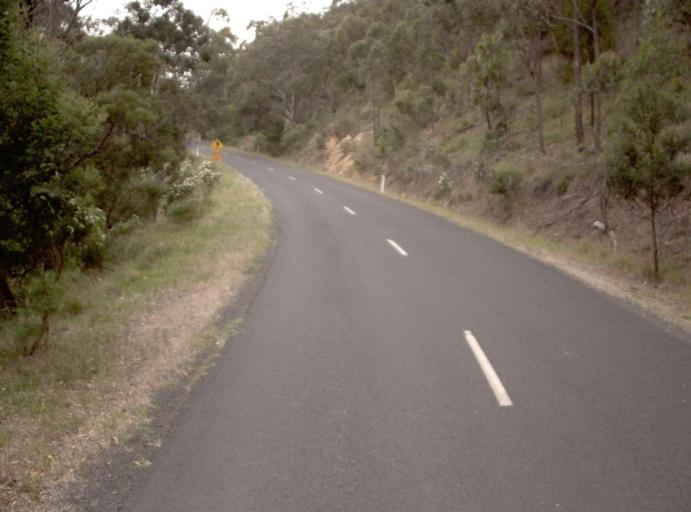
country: AU
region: Victoria
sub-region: East Gippsland
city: Bairnsdale
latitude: -37.4779
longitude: 147.2124
